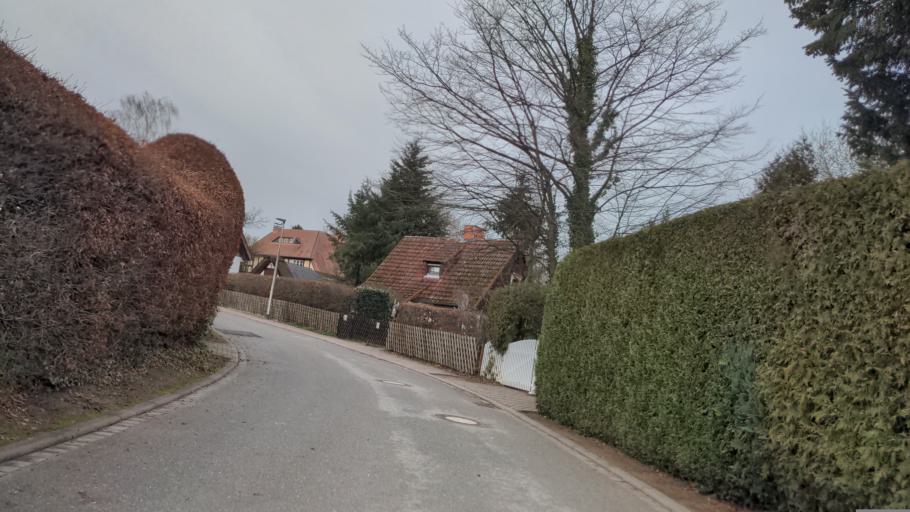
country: DE
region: Schleswig-Holstein
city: Malente
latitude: 54.1689
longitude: 10.5703
